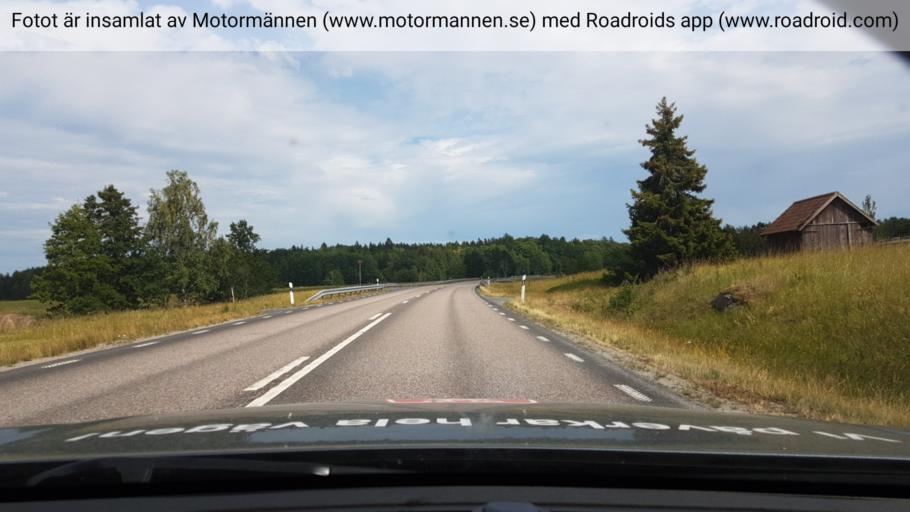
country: SE
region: Uppsala
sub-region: Enkopings Kommun
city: Orsundsbro
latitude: 59.8789
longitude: 17.2791
